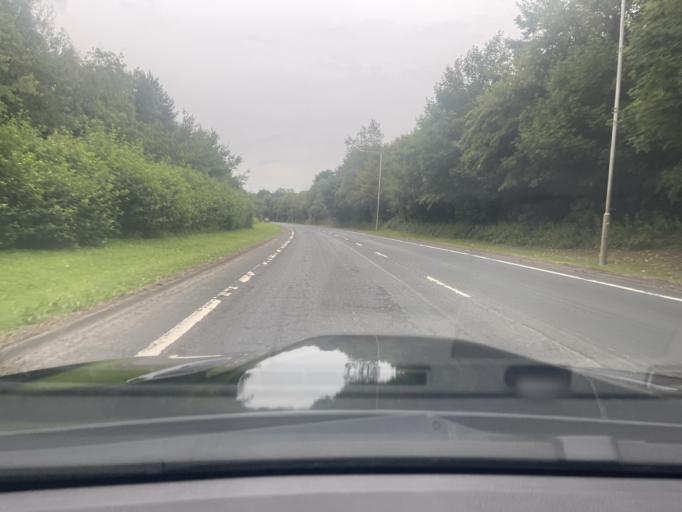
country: GB
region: England
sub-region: Lancashire
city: Leyland
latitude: 53.6984
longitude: -2.7204
